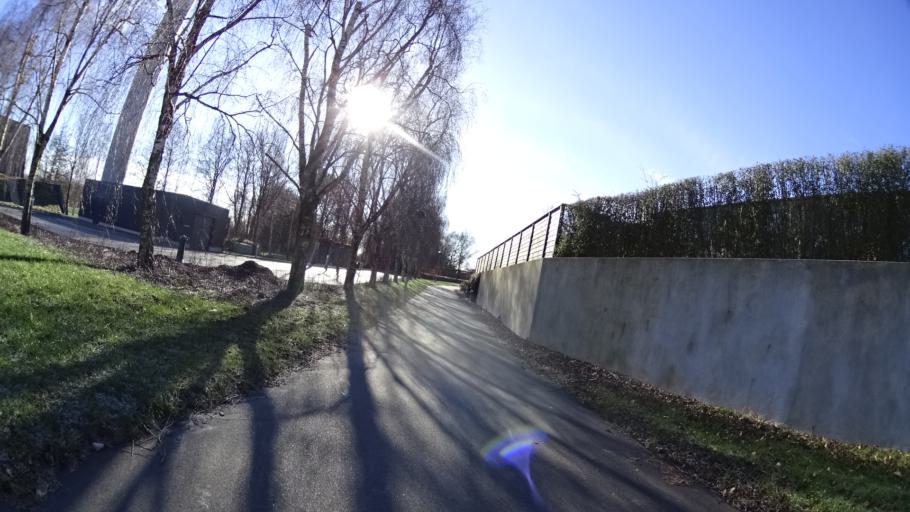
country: DK
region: Central Jutland
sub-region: Arhus Kommune
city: Tranbjerg
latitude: 56.1084
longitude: 10.1019
